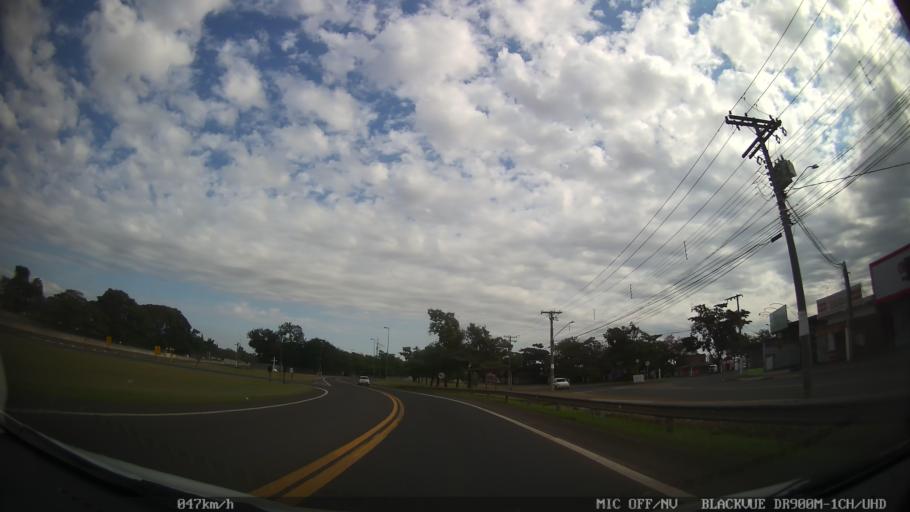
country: BR
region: Sao Paulo
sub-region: Limeira
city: Limeira
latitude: -22.5673
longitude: -47.4404
